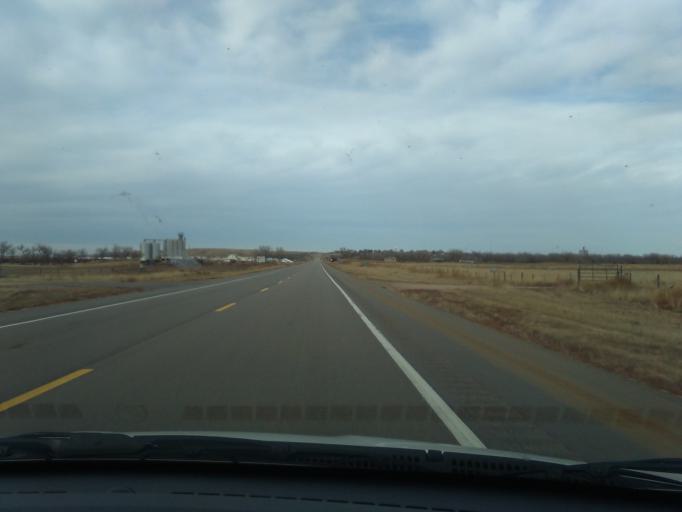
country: US
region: Nebraska
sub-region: Dundy County
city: Benkelman
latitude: 40.0282
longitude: -101.5430
